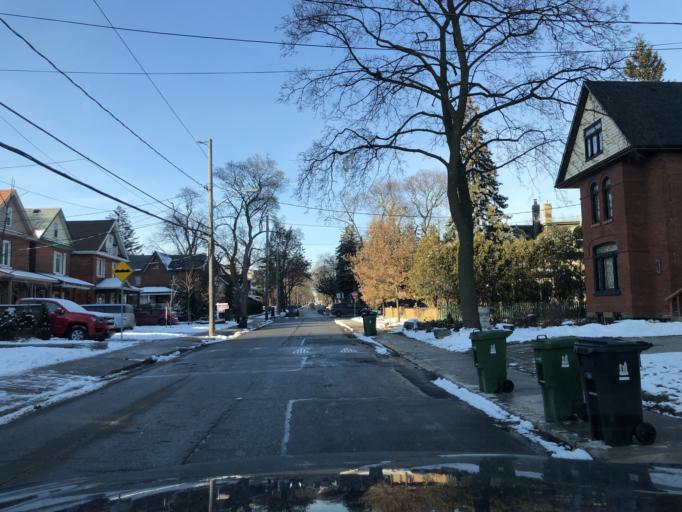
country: CA
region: Ontario
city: Etobicoke
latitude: 43.7033
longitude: -79.5174
